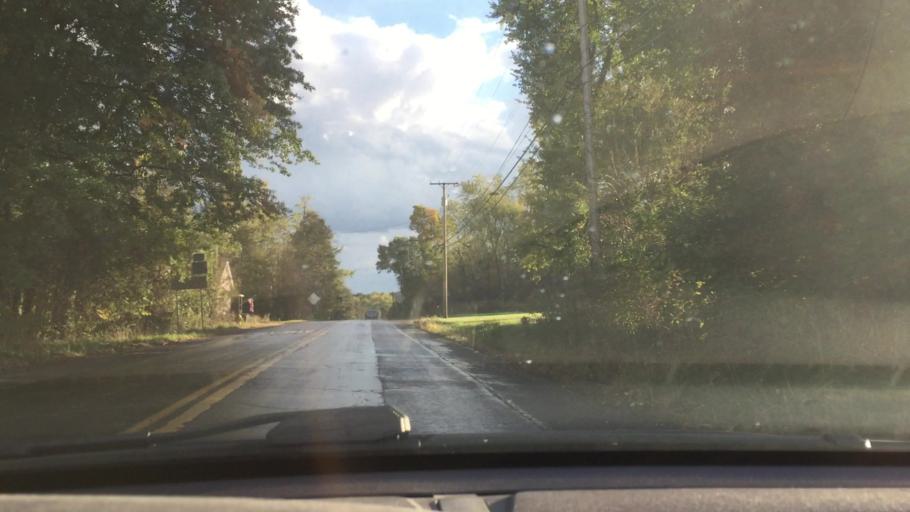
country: US
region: Pennsylvania
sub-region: Lawrence County
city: Oakwood
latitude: 41.0518
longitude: -80.4393
